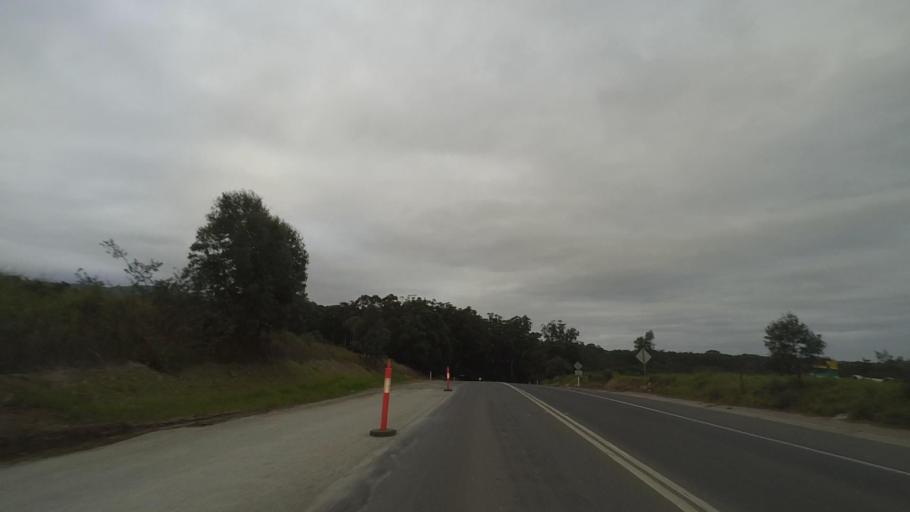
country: AU
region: New South Wales
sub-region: Shoalhaven Shire
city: Berry
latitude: -34.7625
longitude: 150.7252
